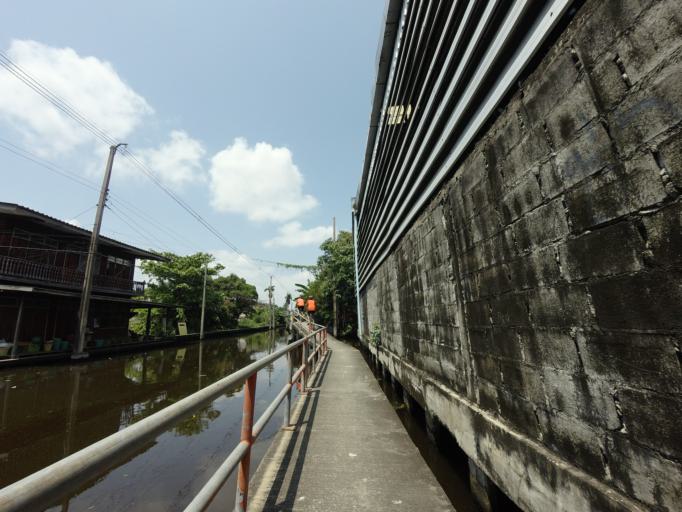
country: TH
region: Bangkok
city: Chom Thong
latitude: 13.6533
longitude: 100.4714
